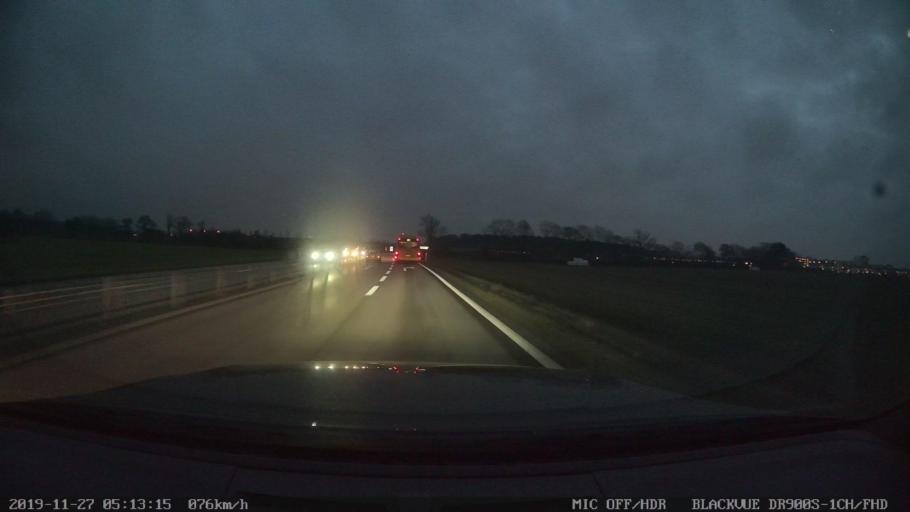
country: SE
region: Skane
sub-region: Helsingborg
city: Odakra
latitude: 56.0871
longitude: 12.7109
